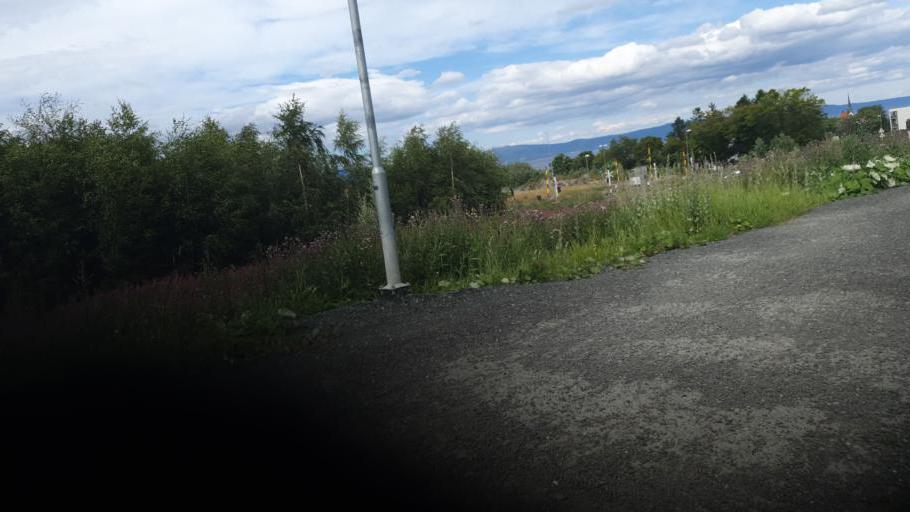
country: NO
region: Sor-Trondelag
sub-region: Klaebu
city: Klaebu
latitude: 63.4241
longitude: 10.5352
